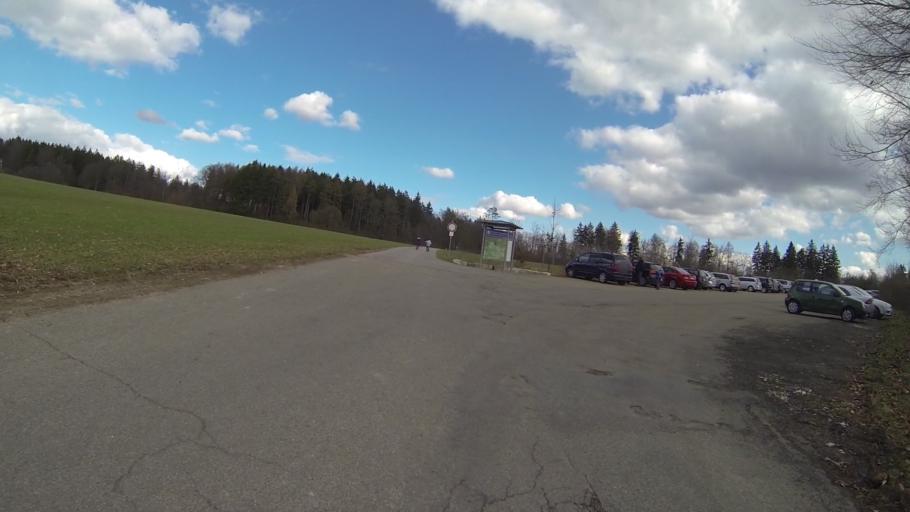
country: DE
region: Baden-Wuerttemberg
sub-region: Regierungsbezirk Stuttgart
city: Steinheim am Albuch
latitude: 48.6967
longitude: 10.1029
